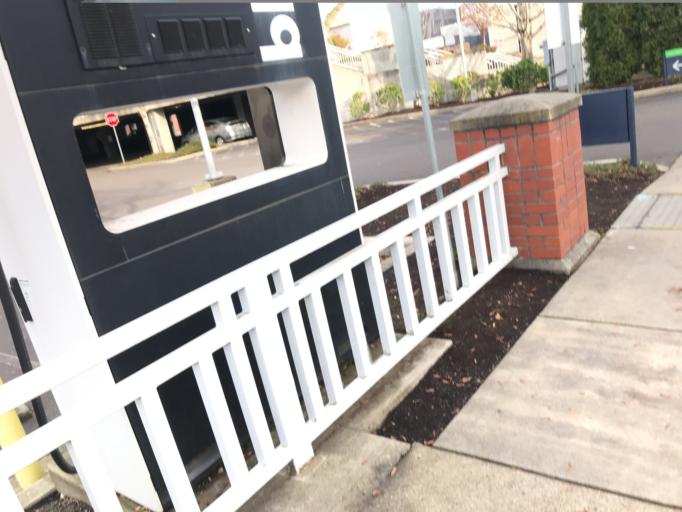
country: US
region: Oregon
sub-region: Washington County
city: Hillsboro
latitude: 45.5215
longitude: -122.9891
